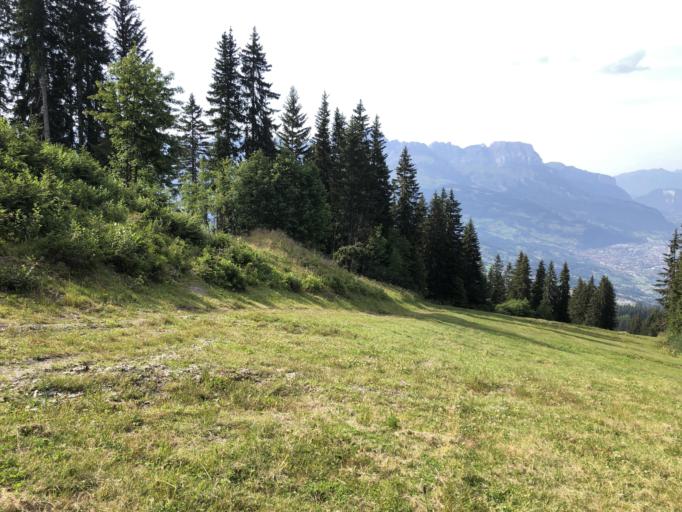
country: FR
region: Rhone-Alpes
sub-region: Departement de la Haute-Savoie
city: Combloux
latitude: 45.8648
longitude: 6.6627
